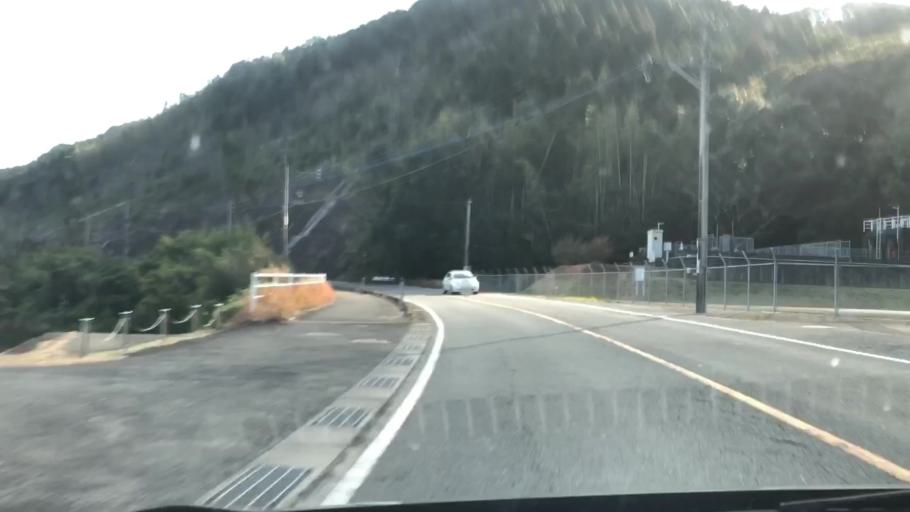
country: JP
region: Kagoshima
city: Satsumasendai
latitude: 31.8580
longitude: 130.3160
